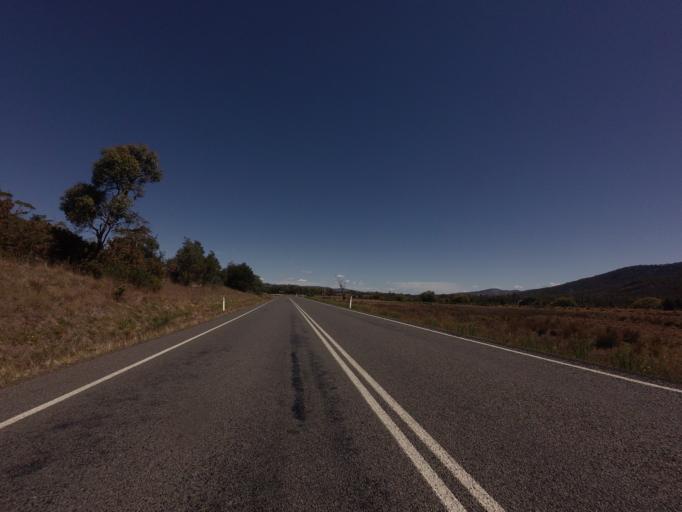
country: AU
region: Tasmania
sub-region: Northern Midlands
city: Evandale
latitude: -41.7464
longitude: 147.7834
